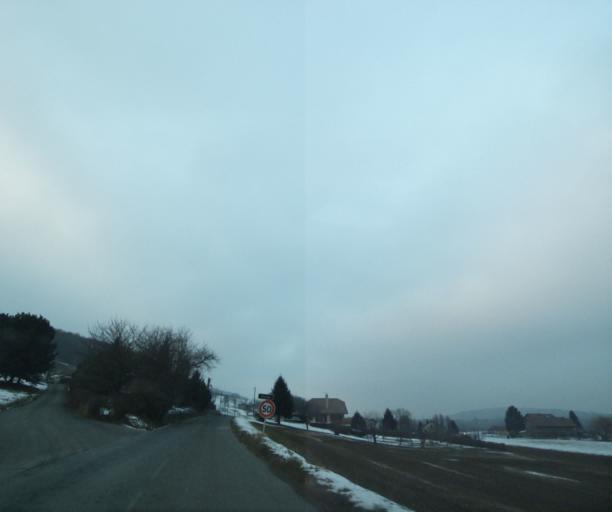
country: FR
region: Rhone-Alpes
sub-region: Departement de la Haute-Savoie
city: Arthaz-Pont-Notre-Dame
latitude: 46.1485
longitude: 6.2464
